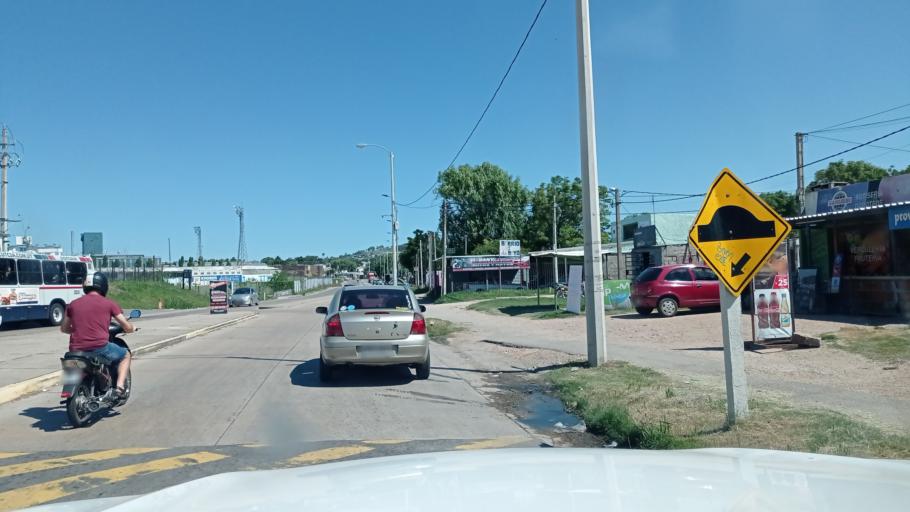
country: UY
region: Montevideo
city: Montevideo
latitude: -34.8648
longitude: -56.2527
